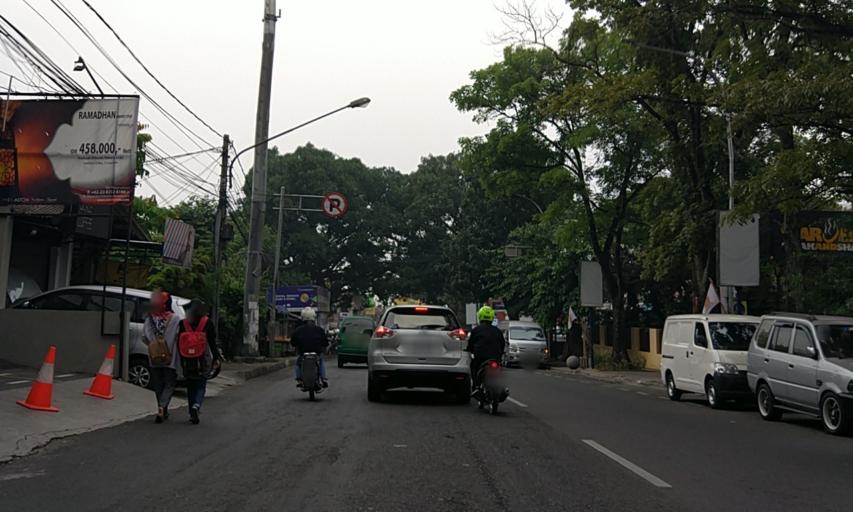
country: ID
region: West Java
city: Bandung
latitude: -6.8899
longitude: 107.6163
